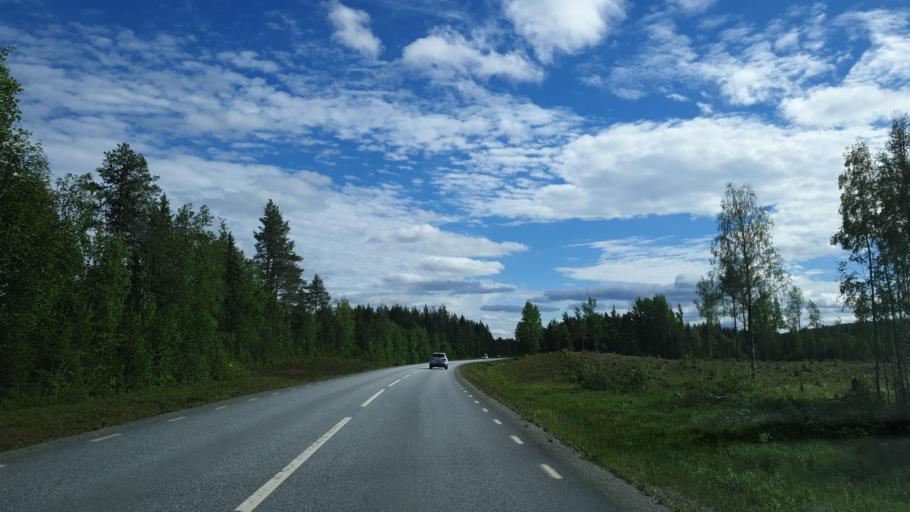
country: SE
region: Vaesterbotten
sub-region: Vilhelmina Kommun
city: Vilhelmina
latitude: 64.5052
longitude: 16.7740
